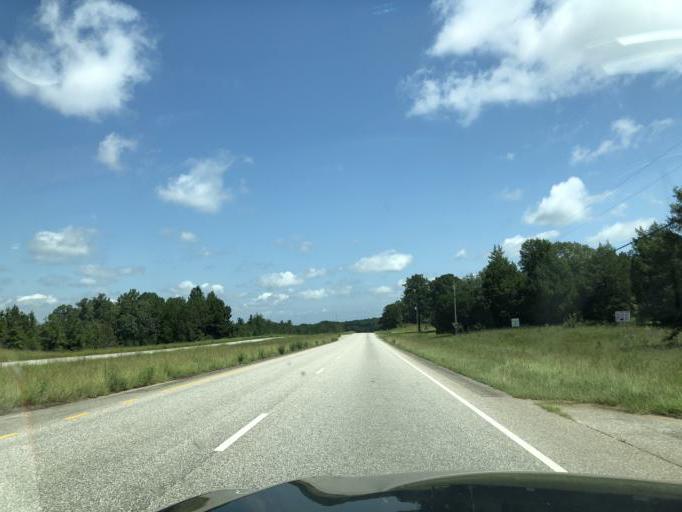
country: US
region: Alabama
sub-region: Henry County
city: Abbeville
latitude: 31.7231
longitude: -85.2638
